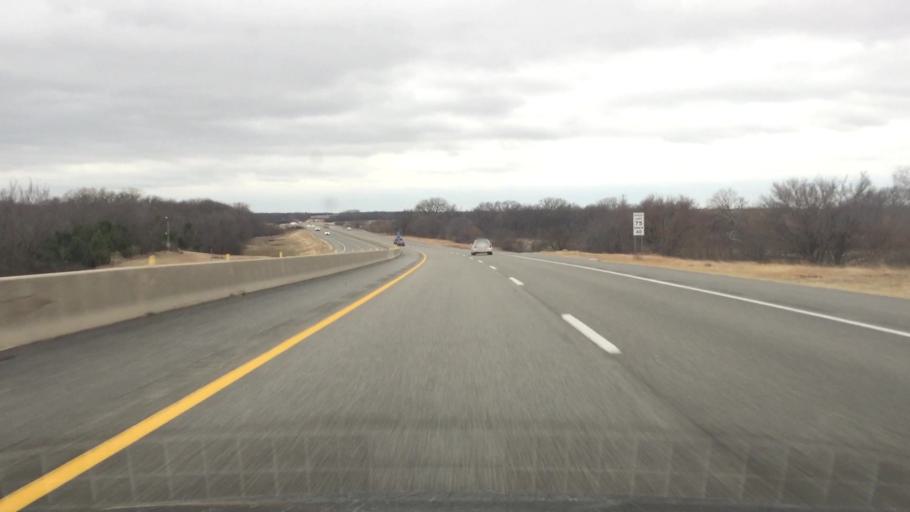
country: US
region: Kansas
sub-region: Butler County
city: Towanda
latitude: 37.7613
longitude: -96.9992
